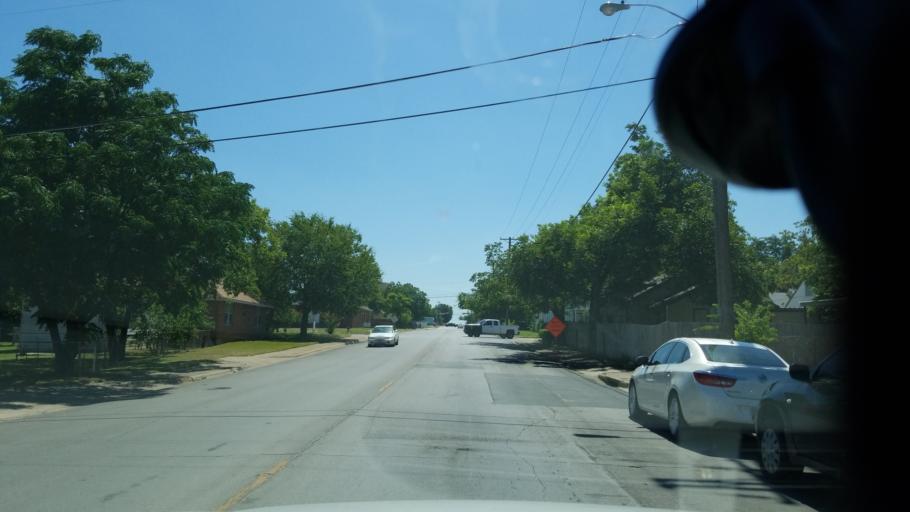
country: US
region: Texas
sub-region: Dallas County
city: Dallas
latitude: 32.7132
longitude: -96.8178
